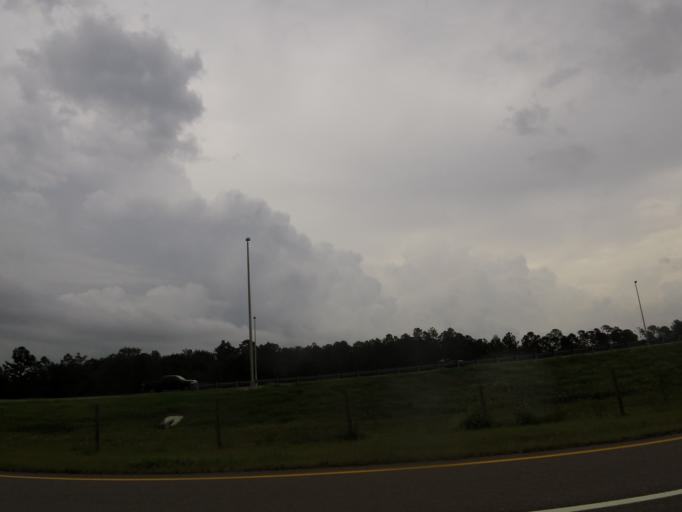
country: US
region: Florida
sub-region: Clay County
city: Middleburg
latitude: 30.1182
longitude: -81.8316
